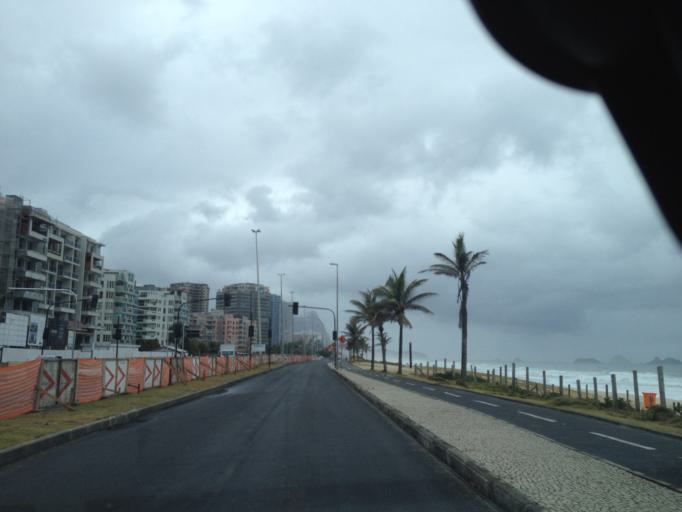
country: BR
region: Rio de Janeiro
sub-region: Rio De Janeiro
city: Rio de Janeiro
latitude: -23.0113
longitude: -43.3731
